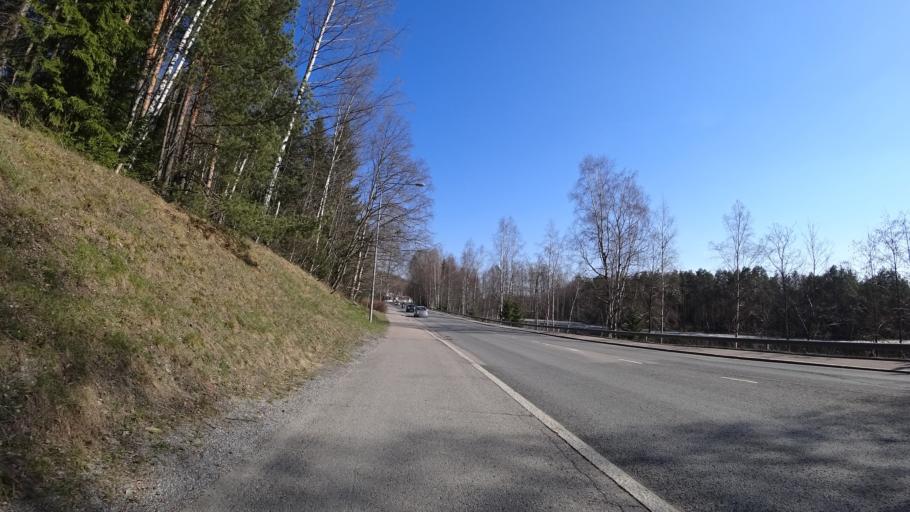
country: FI
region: Pirkanmaa
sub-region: Tampere
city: Pirkkala
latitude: 61.5187
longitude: 23.6447
